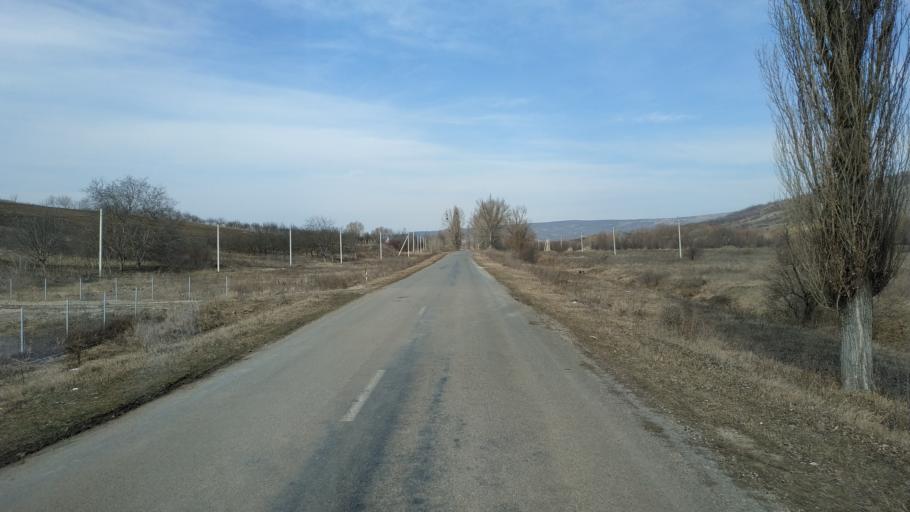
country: MD
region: Nisporeni
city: Nisporeni
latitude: 47.1562
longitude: 28.1069
